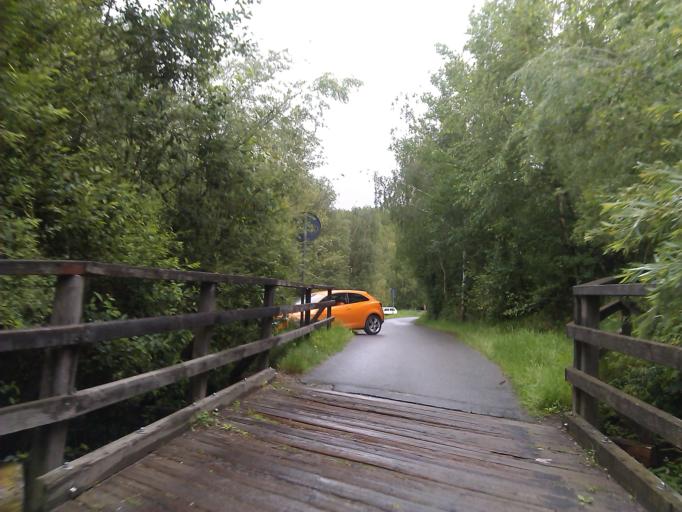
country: IT
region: Trentino-Alto Adige
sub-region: Bolzano
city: Silandro
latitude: 46.6182
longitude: 10.7525
